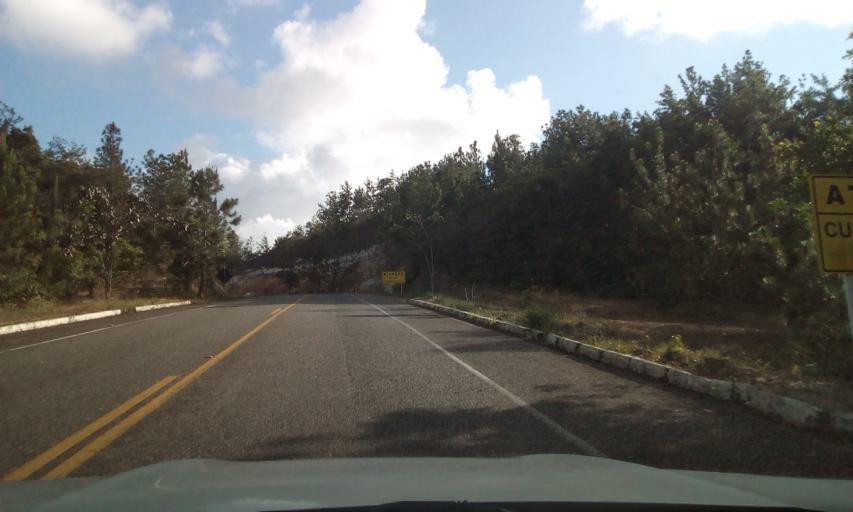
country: BR
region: Bahia
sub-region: Conde
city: Conde
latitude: -12.0968
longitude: -37.7740
